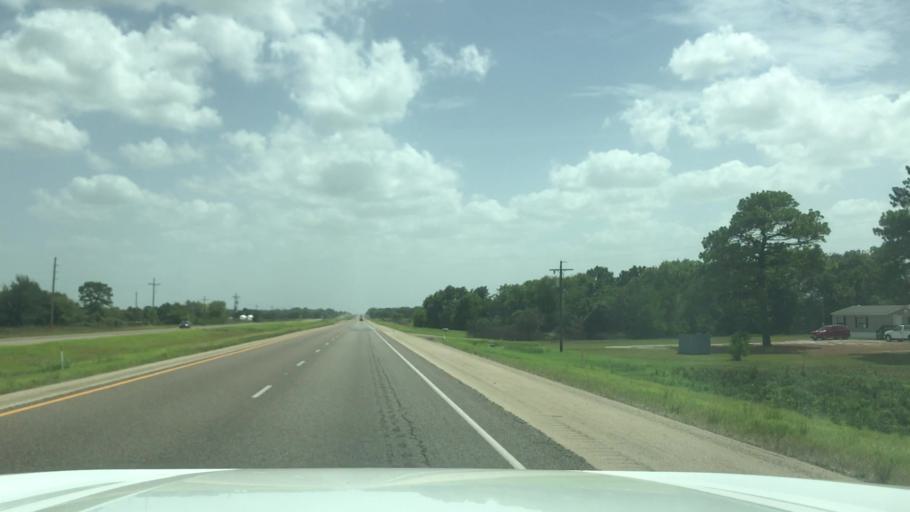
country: US
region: Texas
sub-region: Robertson County
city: Calvert
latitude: 31.0796
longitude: -96.7136
